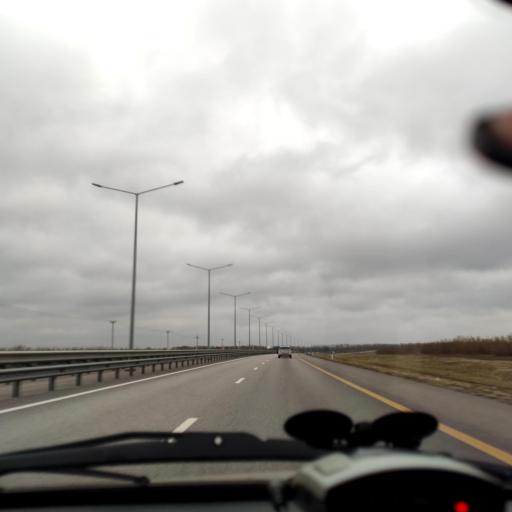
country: RU
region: Voronezj
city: Podkletnoye
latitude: 51.5871
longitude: 39.4457
